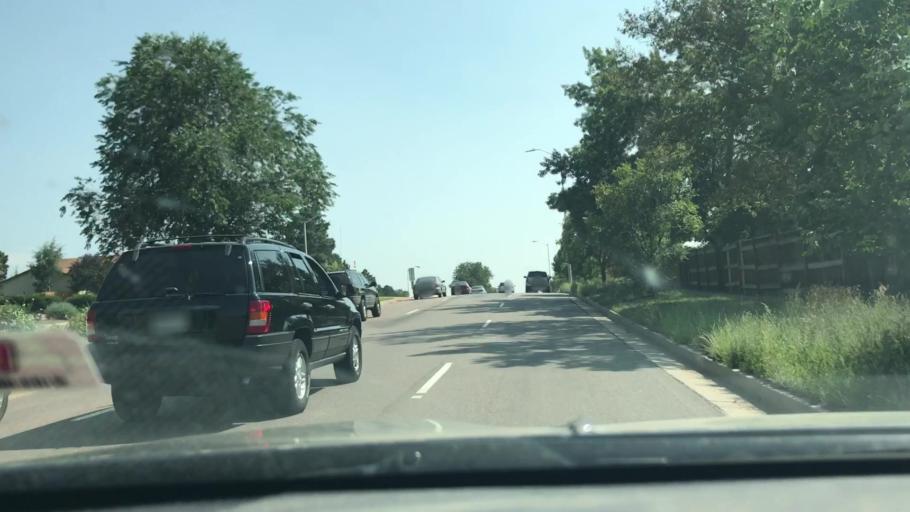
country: US
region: Colorado
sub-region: El Paso County
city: Colorado Springs
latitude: 38.9209
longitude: -104.7754
